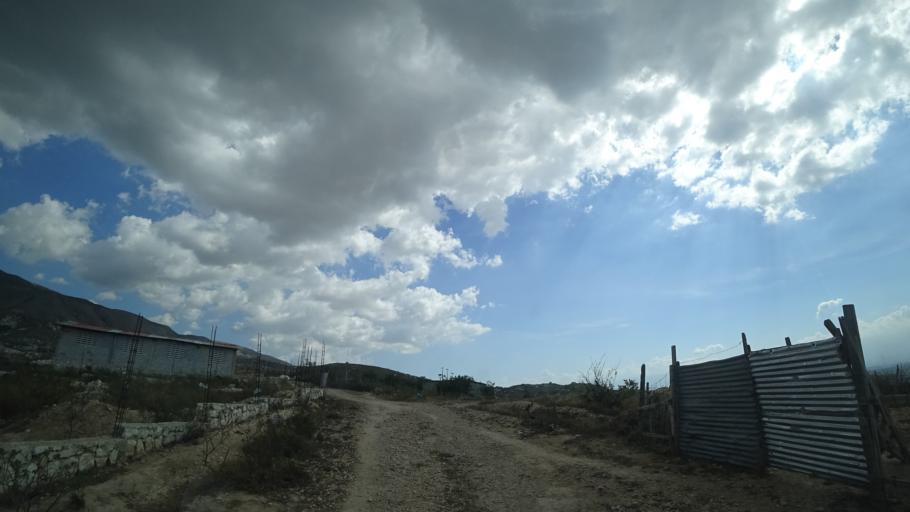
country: HT
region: Ouest
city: Cabaret
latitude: 18.6779
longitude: -72.3093
